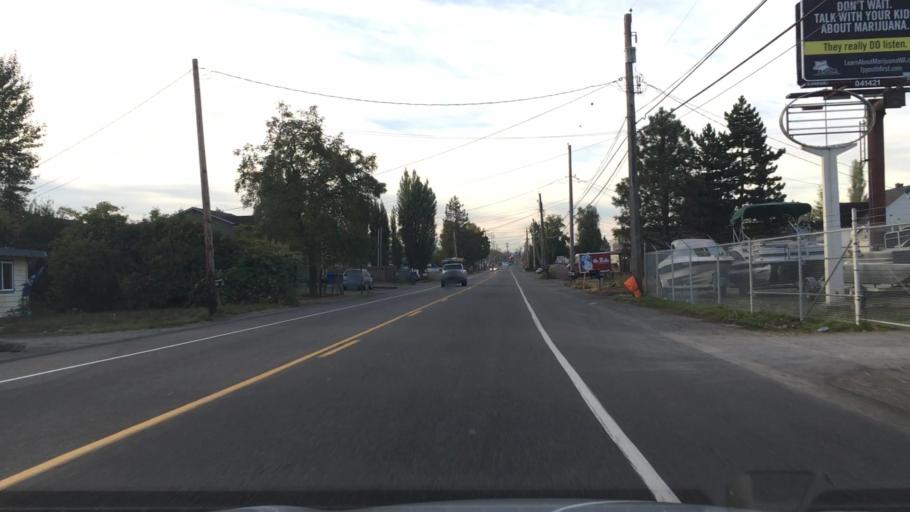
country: US
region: Washington
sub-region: Pierce County
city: Midland
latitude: 47.1722
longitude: -122.4054
